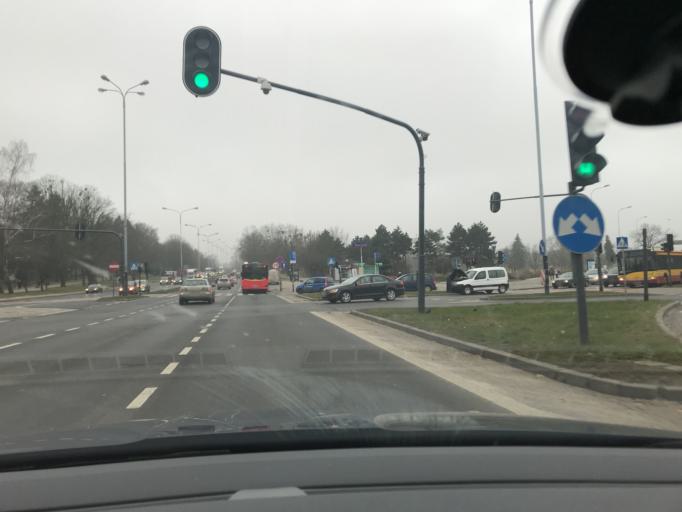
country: PL
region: Lodz Voivodeship
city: Lodz
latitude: 51.7915
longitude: 19.4876
